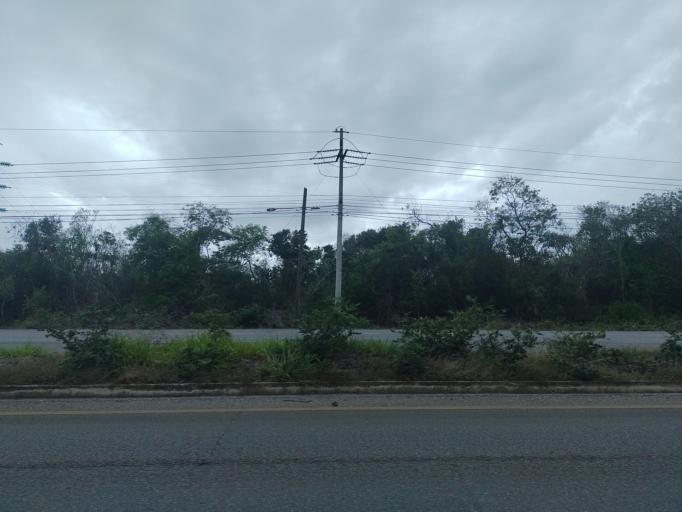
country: MX
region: Quintana Roo
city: Tulum
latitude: 20.2498
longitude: -87.4120
